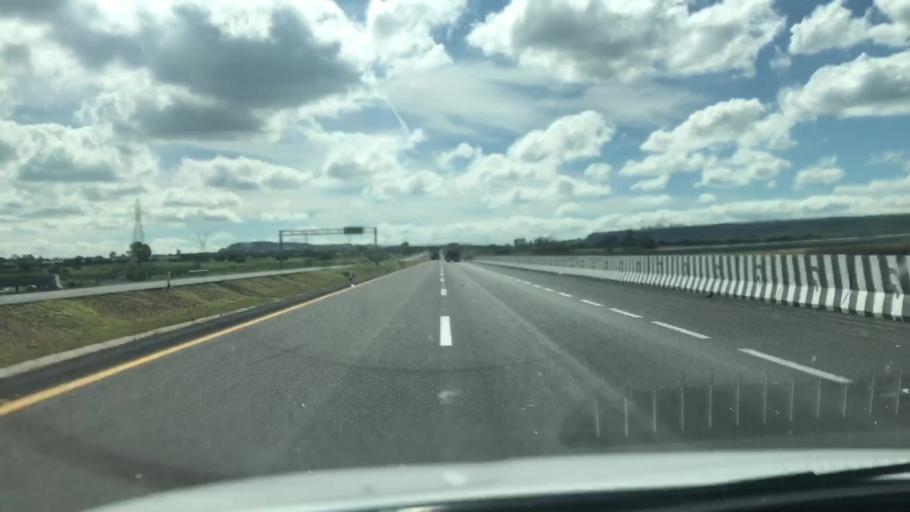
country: MX
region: Guanajuato
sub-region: Silao de la Victoria
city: El Refugio de los Sauces
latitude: 20.9807
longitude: -101.5381
